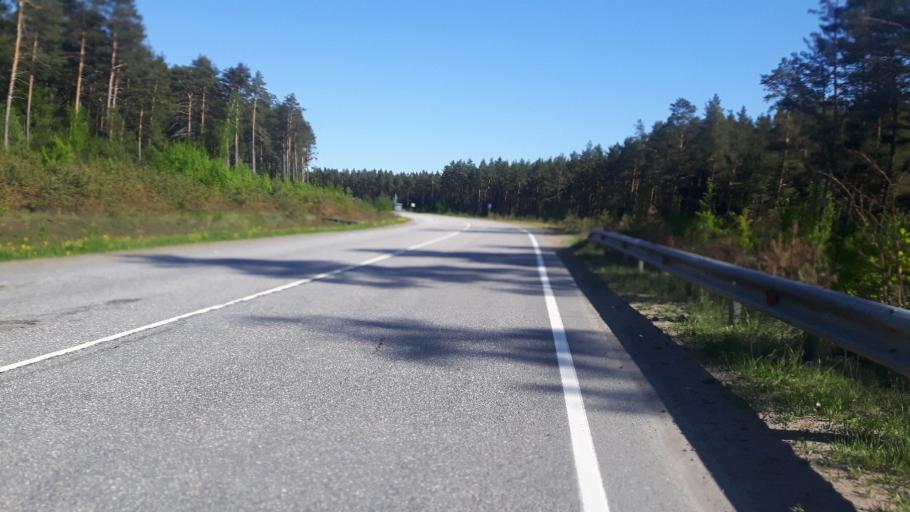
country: RU
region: Leningrad
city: Sosnovyy Bor
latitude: 60.1865
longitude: 29.0253
